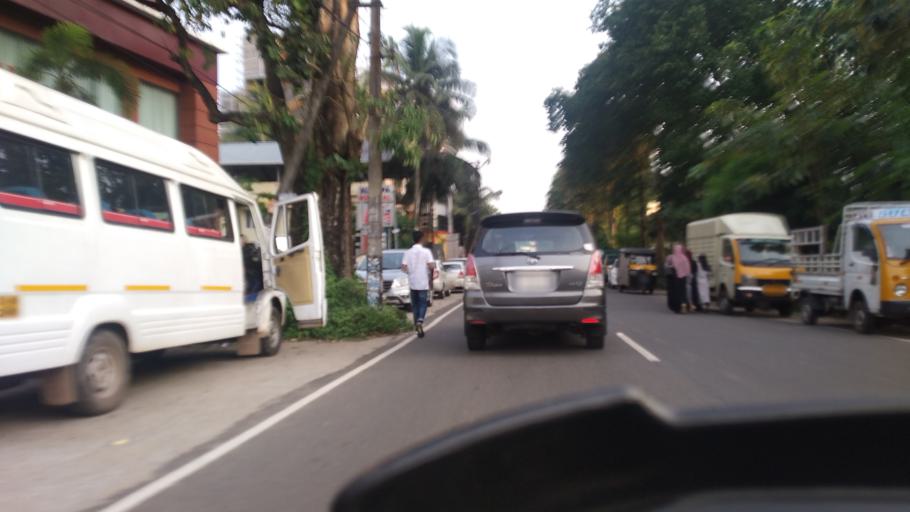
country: IN
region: Kerala
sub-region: Ernakulam
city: Elur
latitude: 10.0304
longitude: 76.3043
